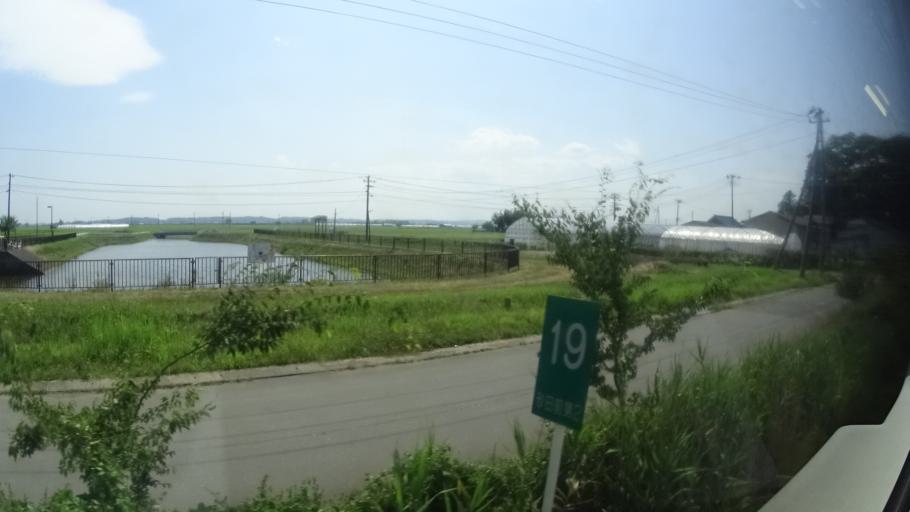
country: JP
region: Miyagi
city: Wakuya
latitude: 38.5298
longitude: 141.1442
